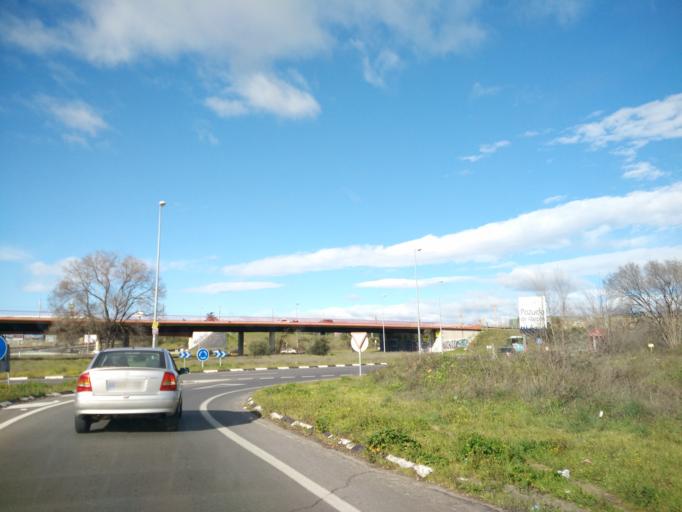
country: ES
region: Madrid
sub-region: Provincia de Madrid
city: Latina
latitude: 40.4003
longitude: -3.7775
